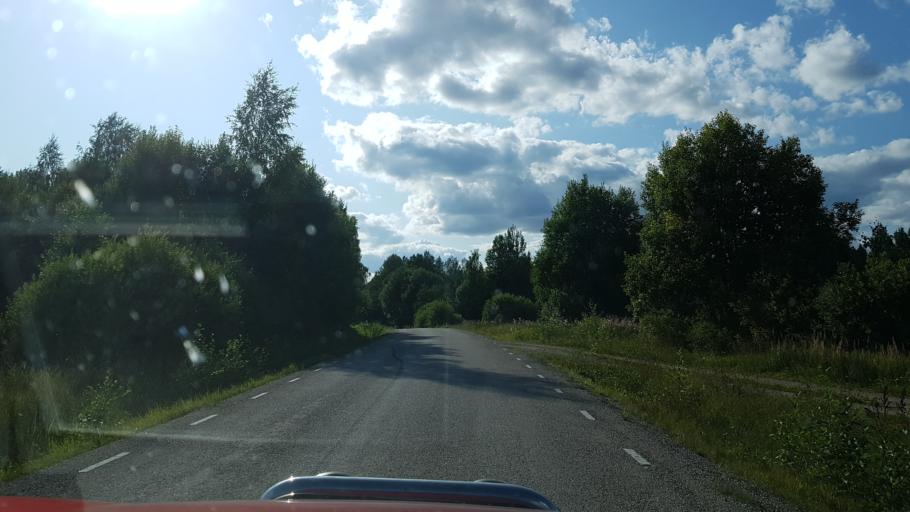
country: EE
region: Vorumaa
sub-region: Voru linn
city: Voru
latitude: 57.9281
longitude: 27.0591
